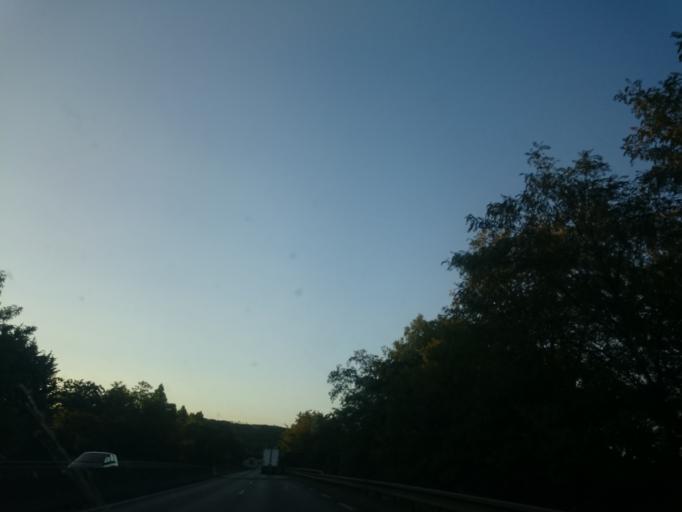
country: FR
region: Ile-de-France
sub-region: Departement de l'Essonne
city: Etrechy
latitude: 48.5002
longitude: 2.2015
